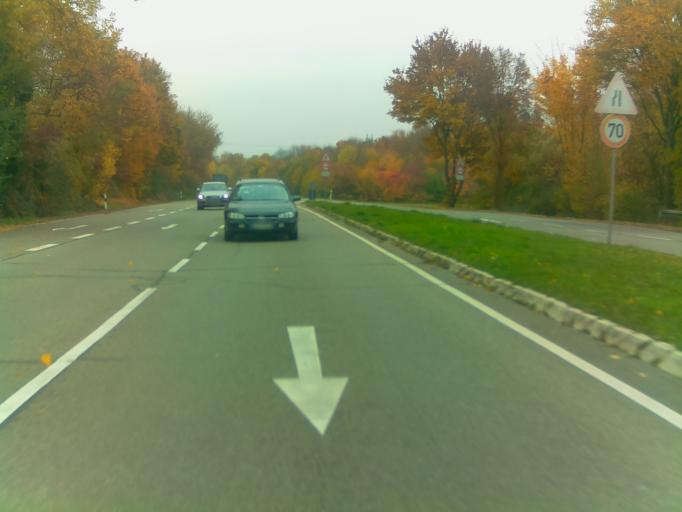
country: DE
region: Baden-Wuerttemberg
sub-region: Karlsruhe Region
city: Ilvesheim
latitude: 49.4798
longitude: 8.5316
